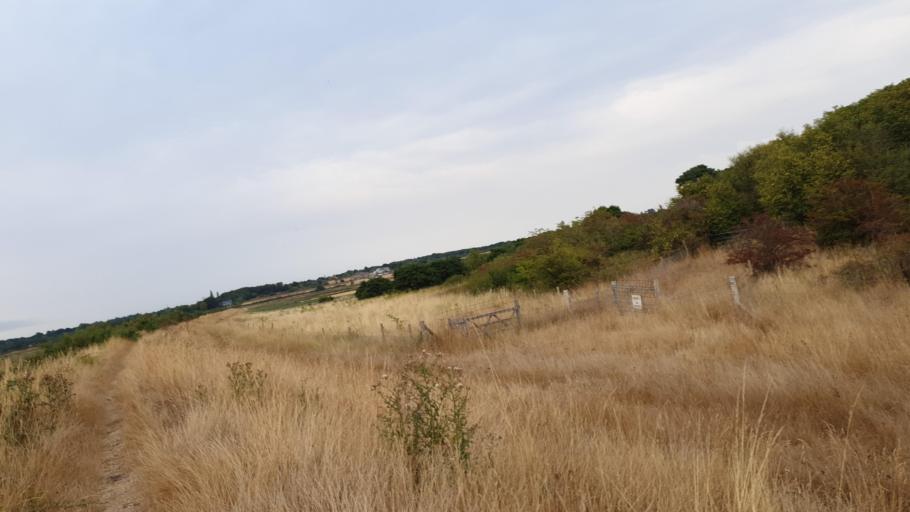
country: GB
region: England
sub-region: Essex
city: Alresford
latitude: 51.8293
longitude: 0.9822
